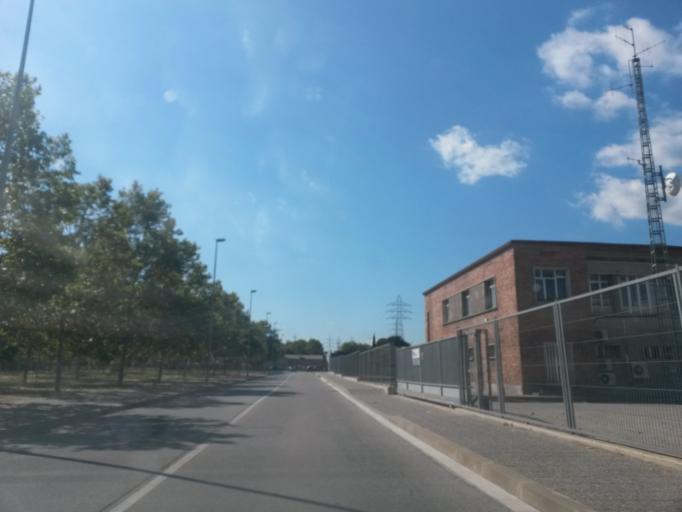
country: ES
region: Catalonia
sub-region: Provincia de Girona
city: Salt
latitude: 41.9696
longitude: 2.8022
